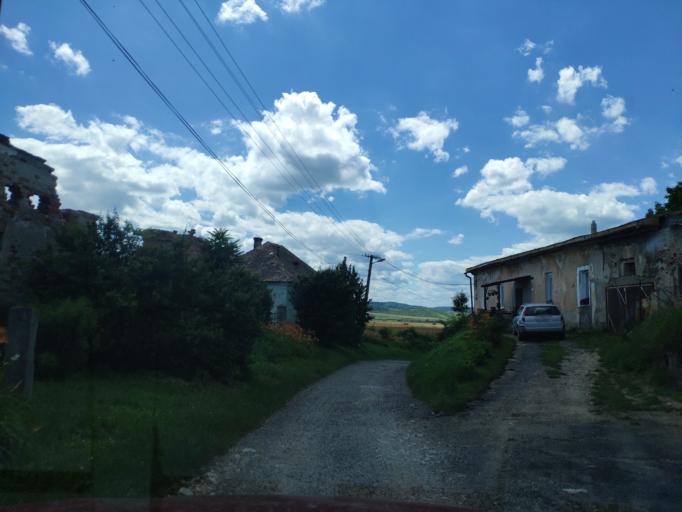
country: HU
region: Borsod-Abauj-Zemplen
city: Ozd
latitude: 48.3031
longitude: 20.2400
